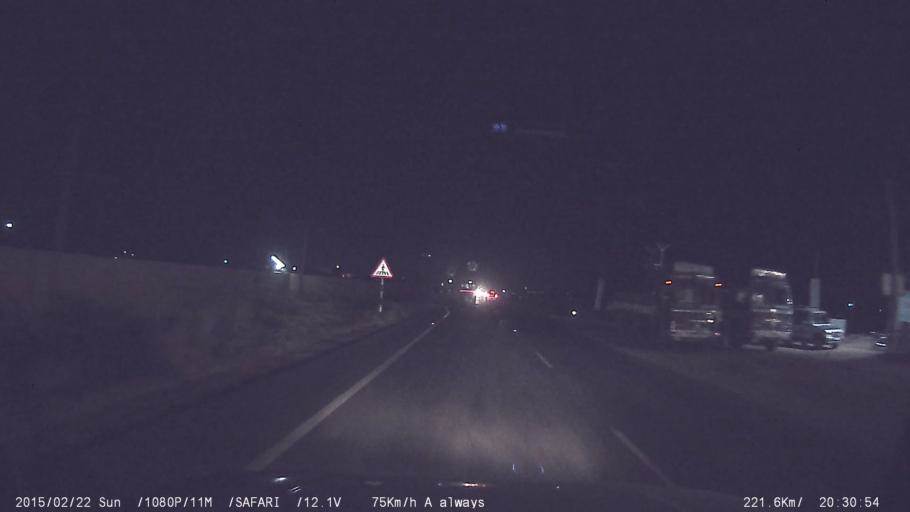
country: IN
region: Tamil Nadu
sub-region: Dindigul
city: Dindigul
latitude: 10.3418
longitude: 77.9432
